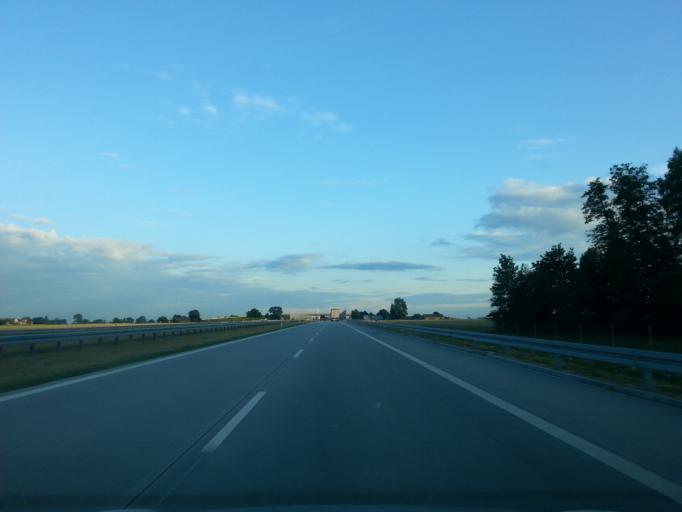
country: PL
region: Lodz Voivodeship
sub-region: Powiat sieradzki
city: Zloczew
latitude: 51.4340
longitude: 18.6457
